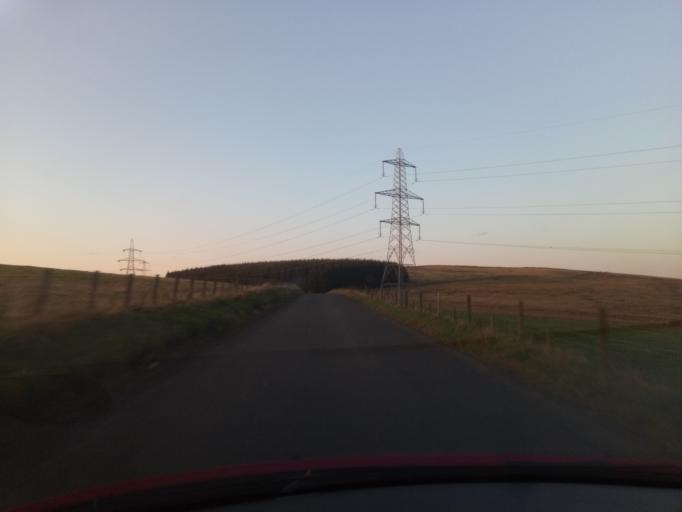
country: GB
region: Scotland
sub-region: East Lothian
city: Pencaitland
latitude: 55.8031
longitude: -2.8874
